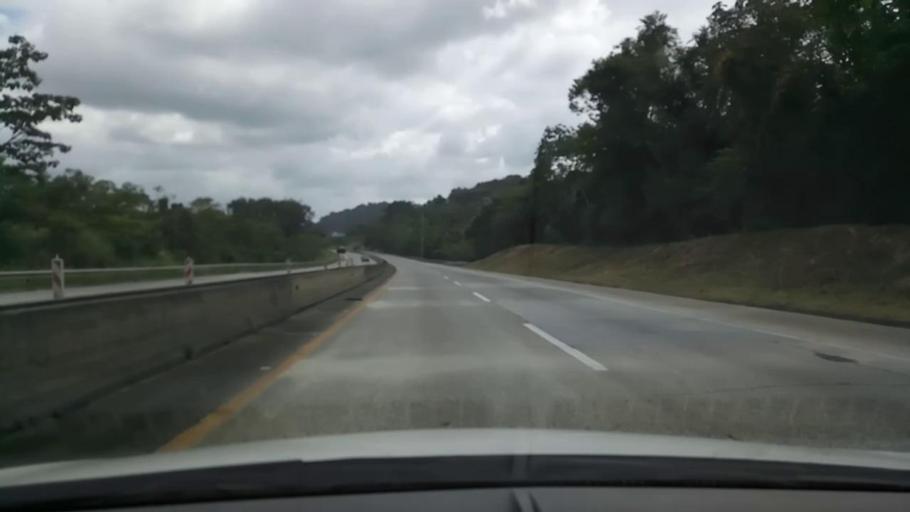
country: PA
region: Panama
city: Chilibre
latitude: 9.1675
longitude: -79.6394
